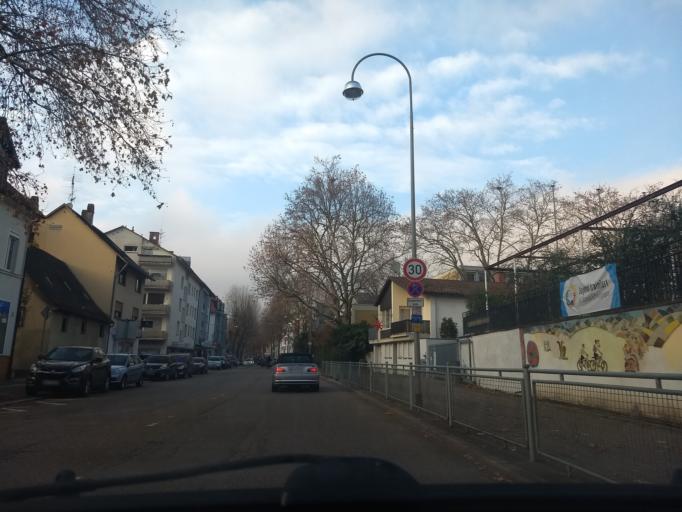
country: DE
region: Baden-Wuerttemberg
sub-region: Karlsruhe Region
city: Baden-Baden
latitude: 48.7765
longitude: 8.2200
